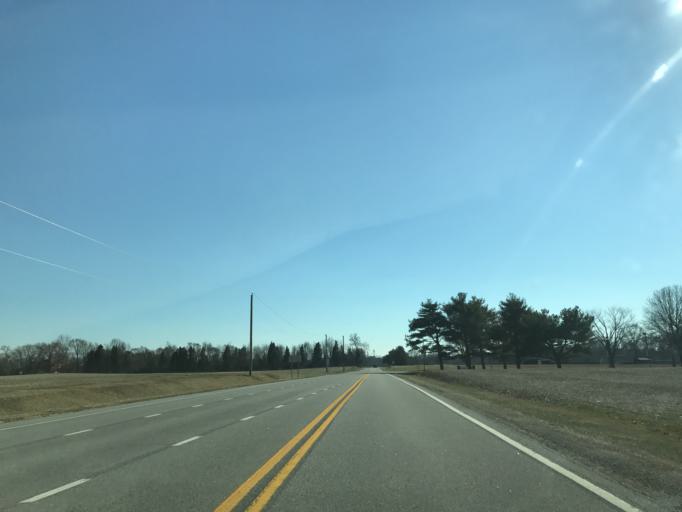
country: US
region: Maryland
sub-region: Queen Anne's County
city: Centreville
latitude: 38.9534
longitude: -76.0786
